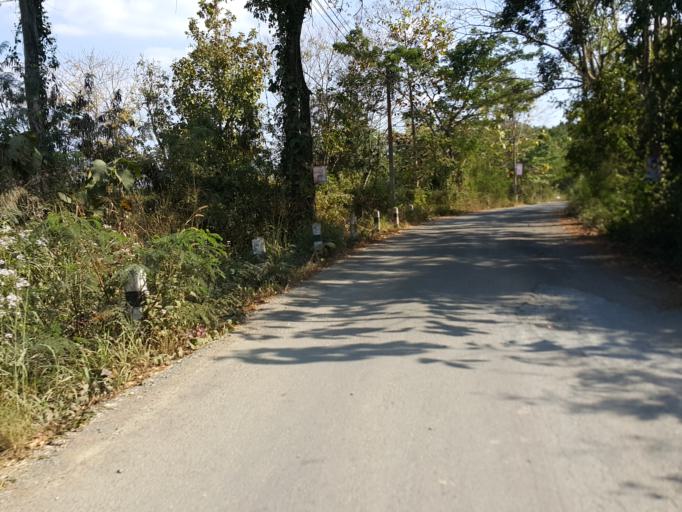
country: TH
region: Chiang Mai
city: Mae On
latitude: 18.7929
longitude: 99.2358
